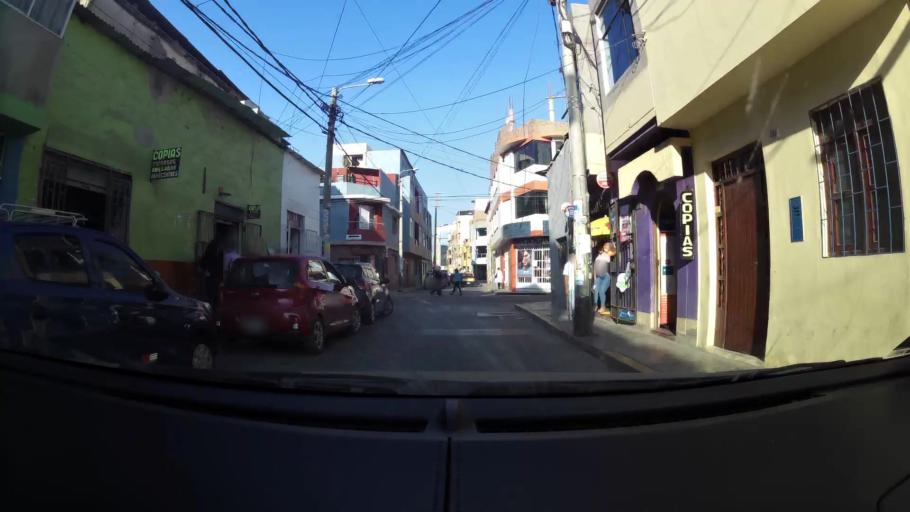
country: PE
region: Lambayeque
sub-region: Provincia de Chiclayo
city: Chiclayo
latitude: -6.7748
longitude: -79.8374
